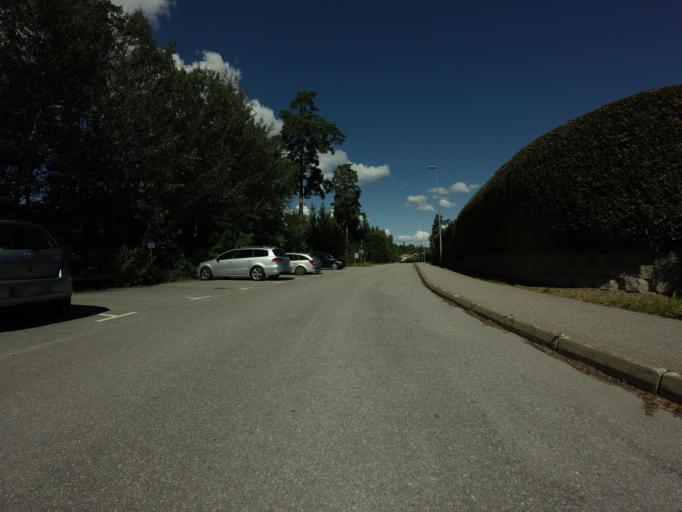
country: SE
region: Stockholm
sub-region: Jarfalla Kommun
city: Jakobsberg
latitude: 59.4566
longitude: 17.8881
